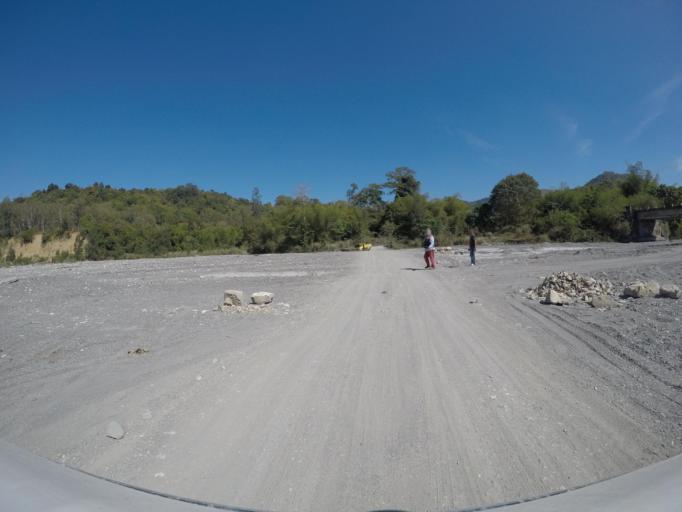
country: TL
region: Manufahi
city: Same
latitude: -8.9583
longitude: 126.0071
